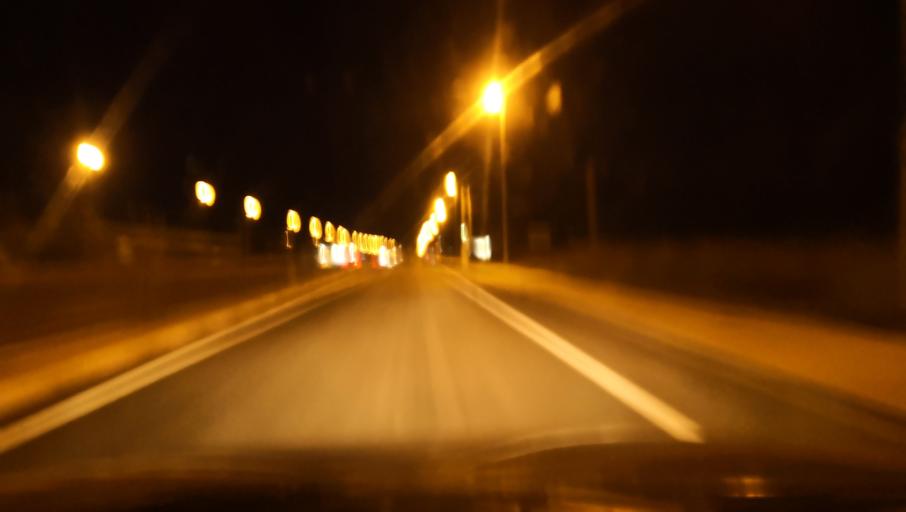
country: ES
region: Castille and Leon
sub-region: Provincia de Zamora
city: Zamora
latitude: 41.5232
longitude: -5.7564
